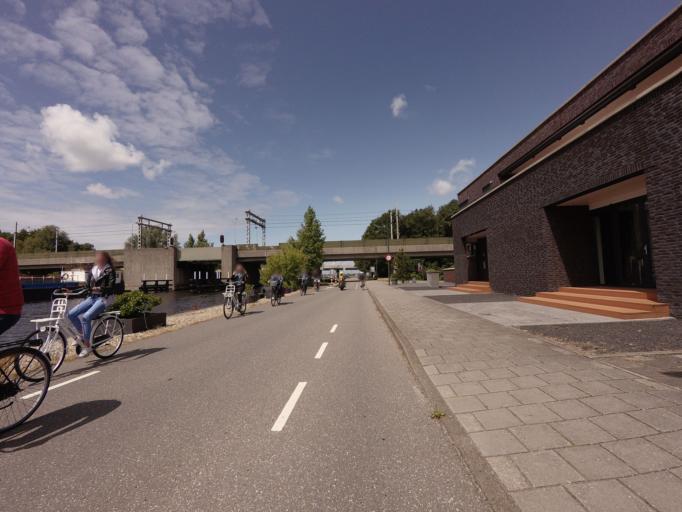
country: NL
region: South Holland
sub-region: Gemeente Teylingen
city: Sassenheim
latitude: 52.2232
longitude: 4.5539
